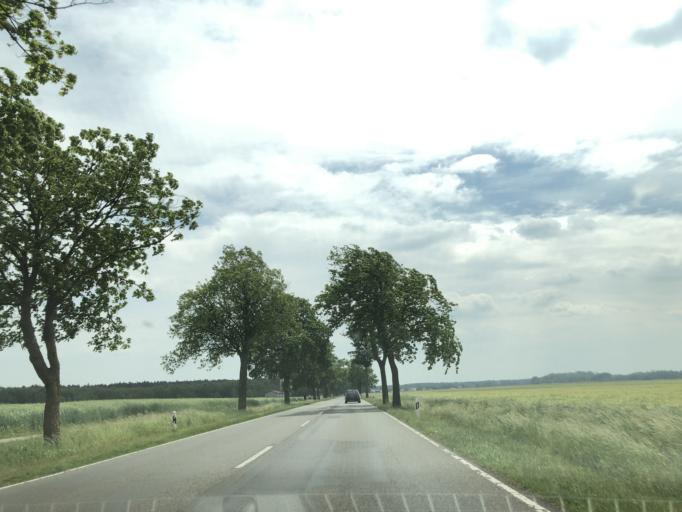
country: DE
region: Brandenburg
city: Kyritz
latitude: 52.9291
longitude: 12.4168
